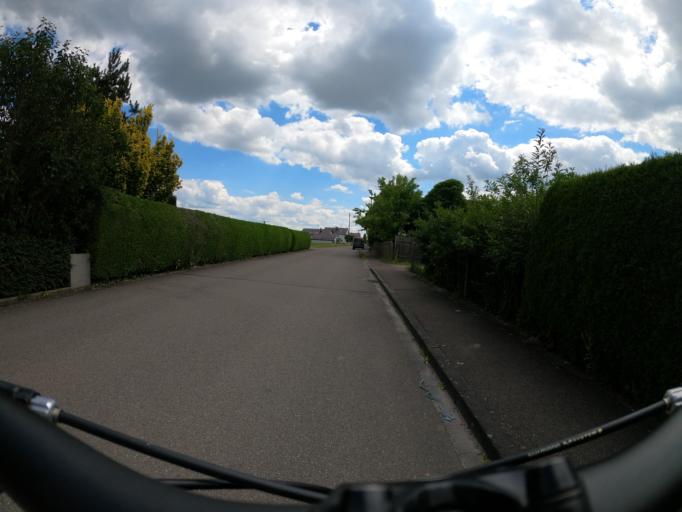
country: DE
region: Bavaria
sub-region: Swabia
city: Pfaffenhofen an der Roth
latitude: 48.3808
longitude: 10.1508
